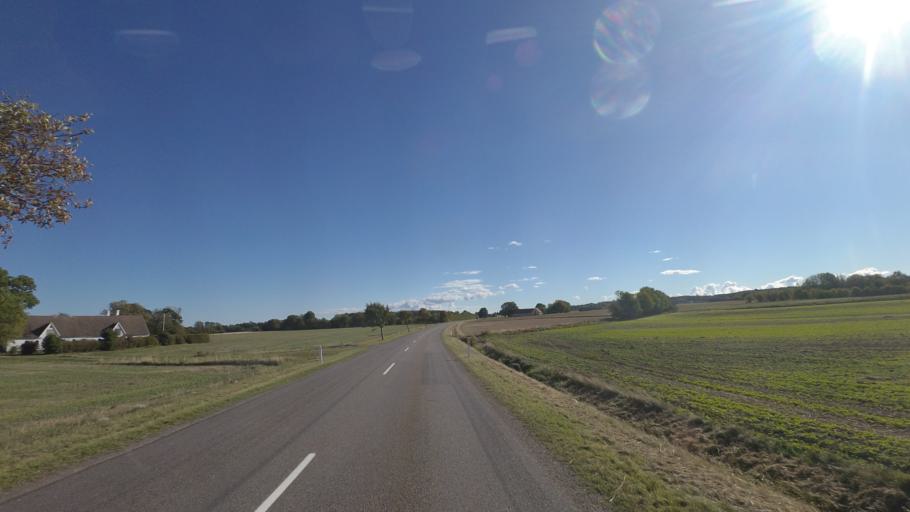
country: DK
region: Capital Region
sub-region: Bornholm Kommune
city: Nexo
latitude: 55.1150
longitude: 15.1080
